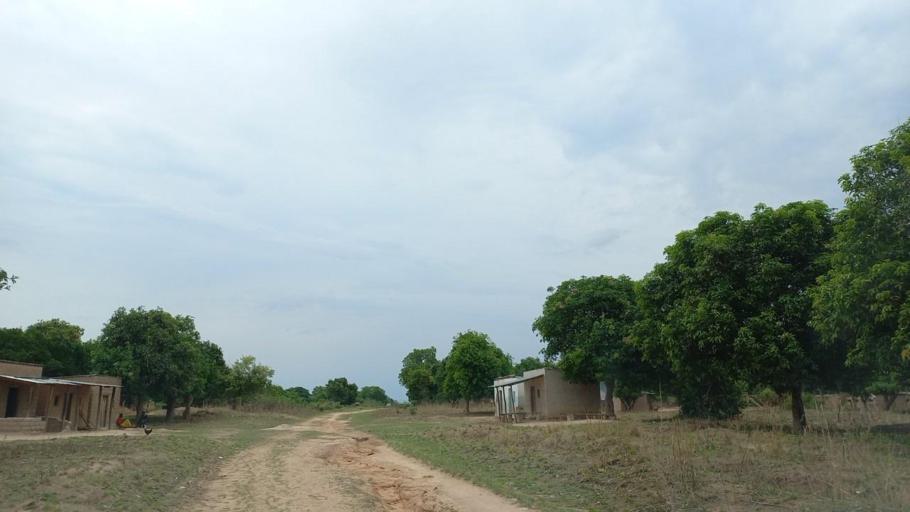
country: ZM
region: North-Western
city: Kalengwa
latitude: -13.6427
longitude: 24.9805
